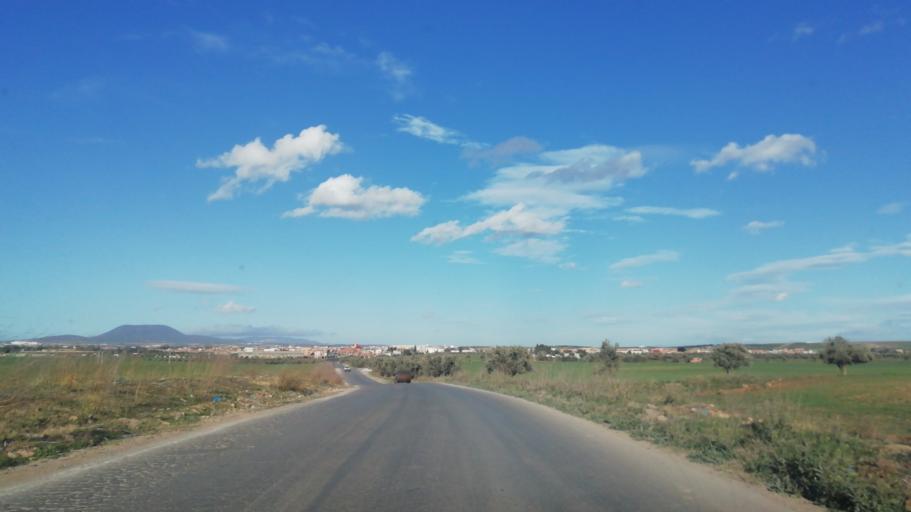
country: DZ
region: Oran
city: Sidi ech Chahmi
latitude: 35.6469
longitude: -0.5330
